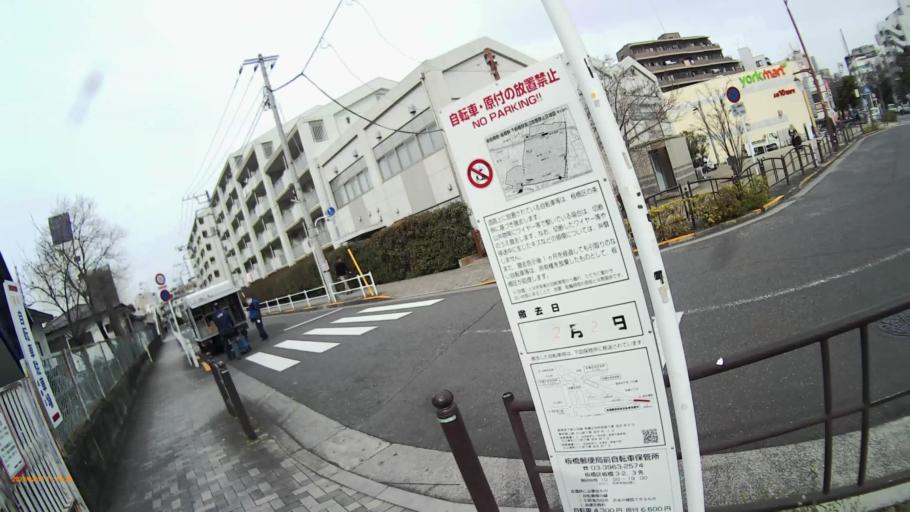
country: JP
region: Saitama
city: Kawaguchi
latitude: 35.7458
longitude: 139.7147
